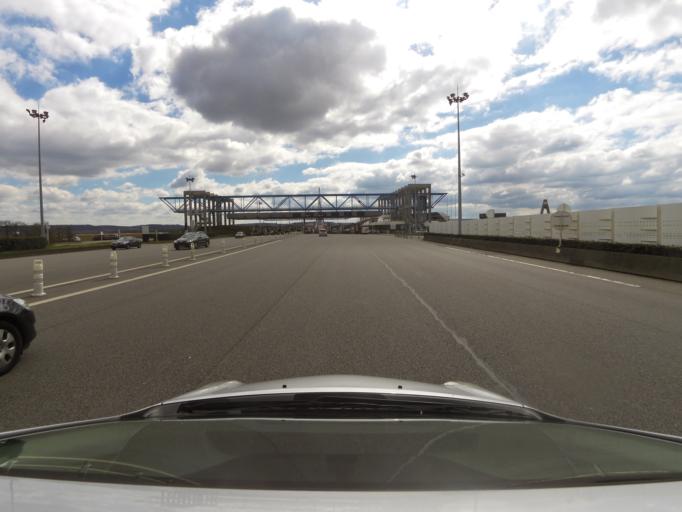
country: FR
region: Lower Normandy
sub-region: Departement du Calvados
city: La Riviere-Saint-Sauveur
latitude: 49.4513
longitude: 0.2713
